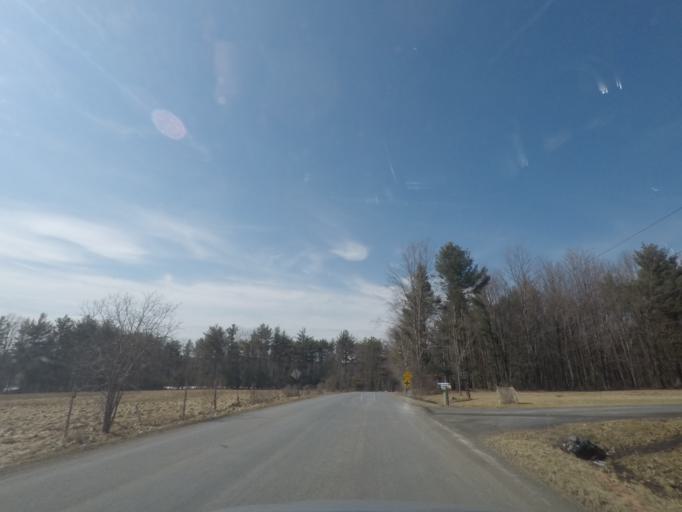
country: US
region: New York
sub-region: Rensselaer County
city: Averill Park
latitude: 42.6114
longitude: -73.5483
